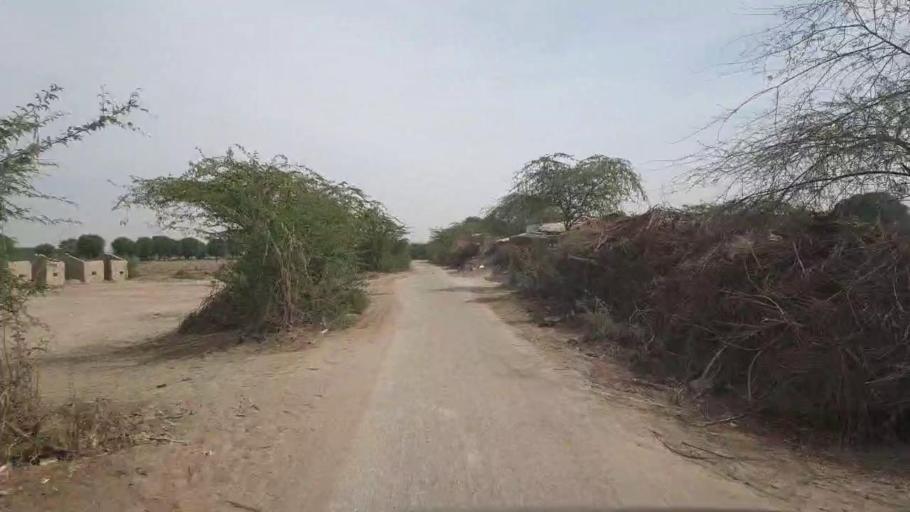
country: PK
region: Sindh
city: Umarkot
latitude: 25.2528
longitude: 69.7090
